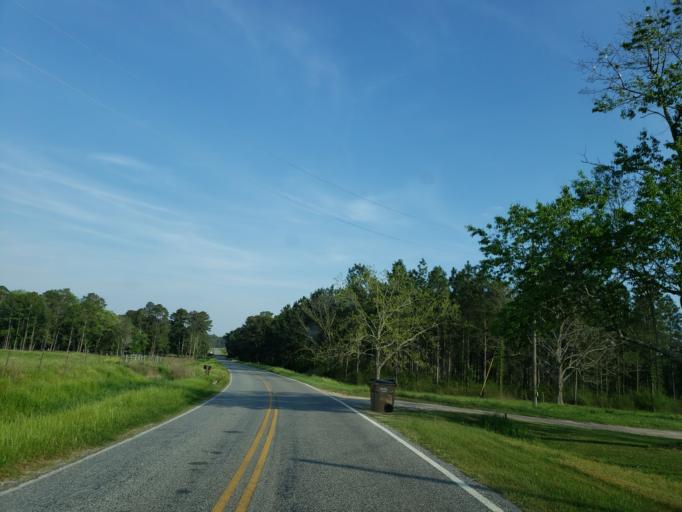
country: US
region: Georgia
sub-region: Tift County
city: Tifton
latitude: 31.4996
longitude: -83.5589
